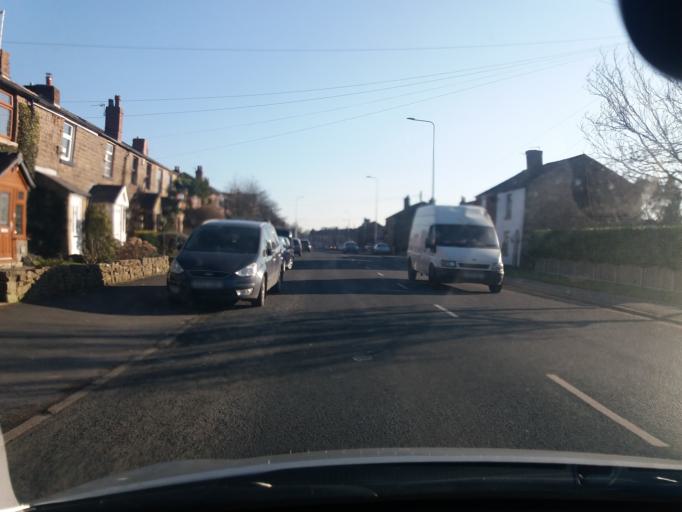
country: GB
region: England
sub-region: Lancashire
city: Adlington
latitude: 53.6243
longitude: -2.6069
